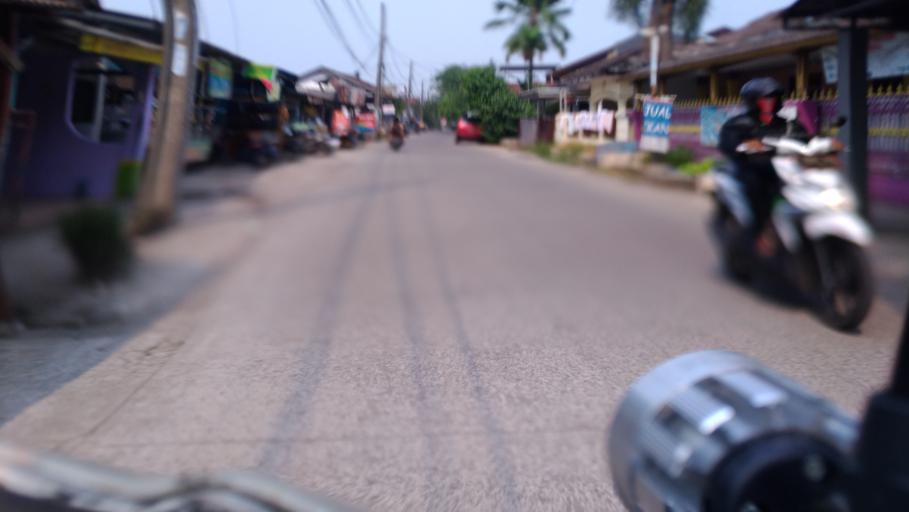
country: ID
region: West Java
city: Depok
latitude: -6.3616
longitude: 106.8723
